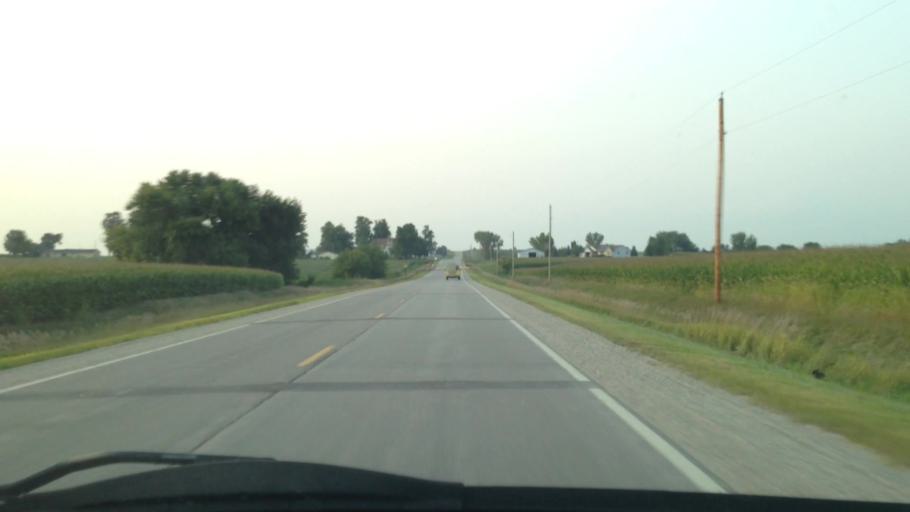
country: US
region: Iowa
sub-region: Benton County
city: Atkins
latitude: 42.0024
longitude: -91.8735
